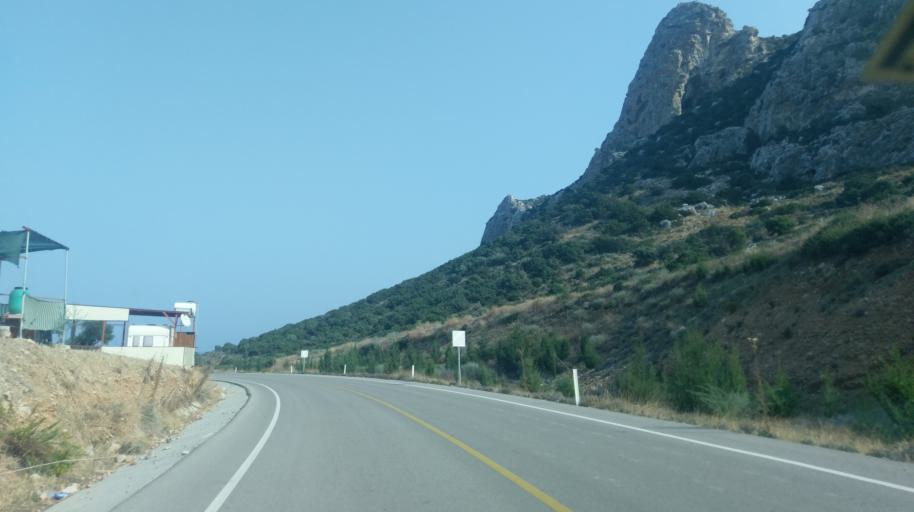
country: CY
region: Ammochostos
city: Leonarisso
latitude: 35.4673
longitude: 34.0334
